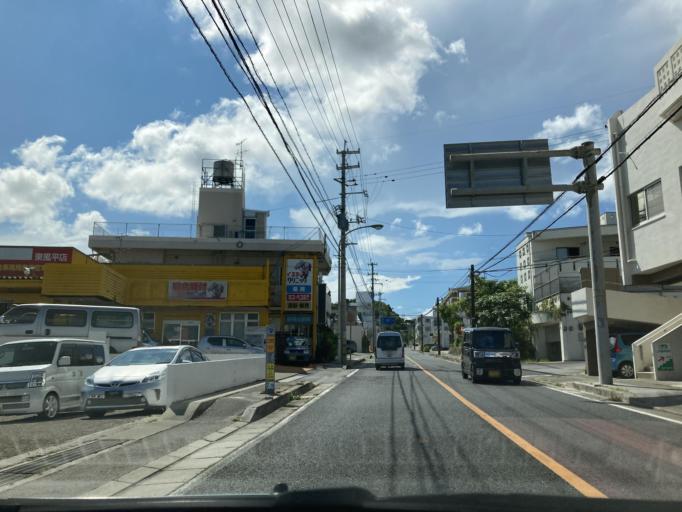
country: JP
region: Okinawa
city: Tomigusuku
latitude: 26.1756
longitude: 127.7188
